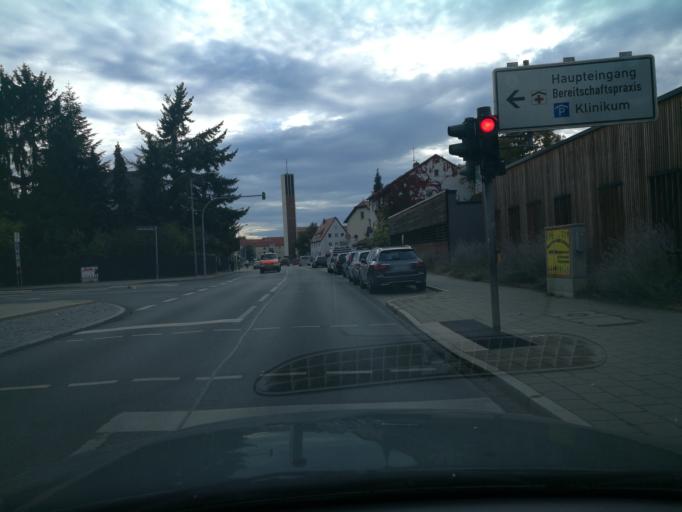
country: DE
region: Bavaria
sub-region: Regierungsbezirk Mittelfranken
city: Furth
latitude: 49.4842
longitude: 10.9714
